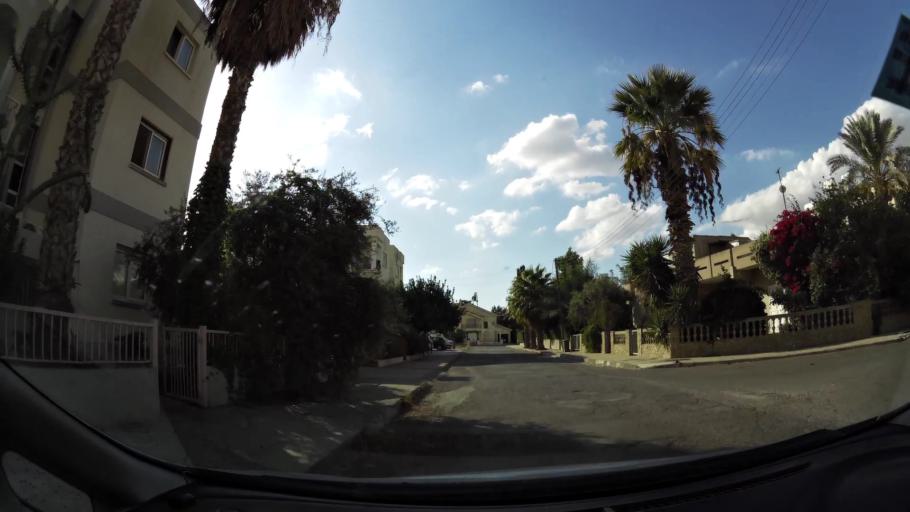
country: CY
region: Lefkosia
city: Nicosia
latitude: 35.1954
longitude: 33.3603
